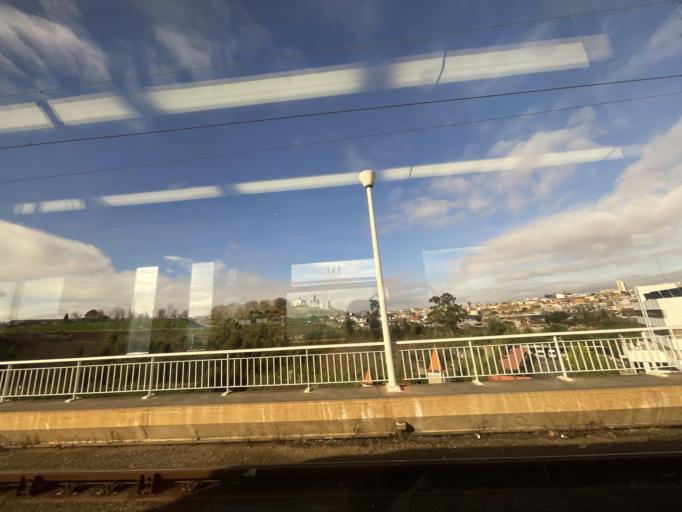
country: PT
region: Porto
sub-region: Porto
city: Porto
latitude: 41.1367
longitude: -8.5987
